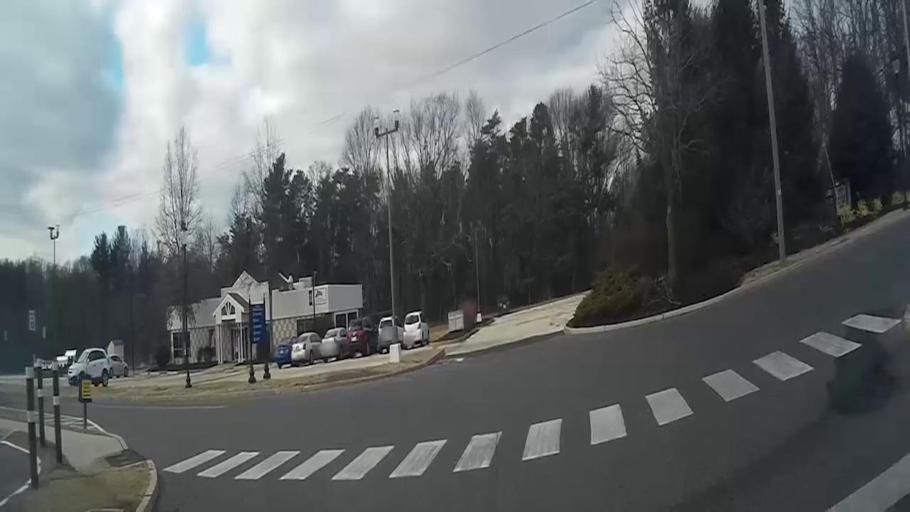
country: US
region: New Jersey
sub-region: Gloucester County
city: Turnersville
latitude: 39.7872
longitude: -75.0361
